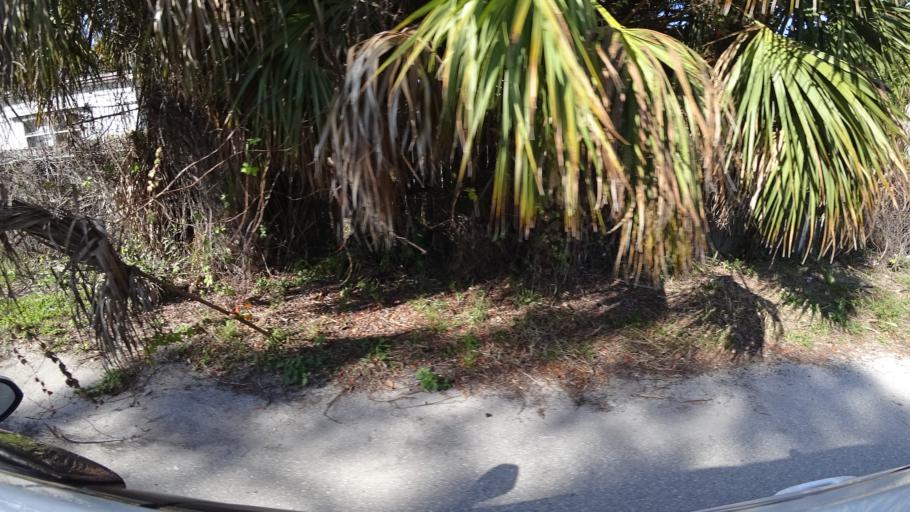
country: US
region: Florida
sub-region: Manatee County
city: Bayshore Gardens
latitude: 27.4359
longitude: -82.5737
